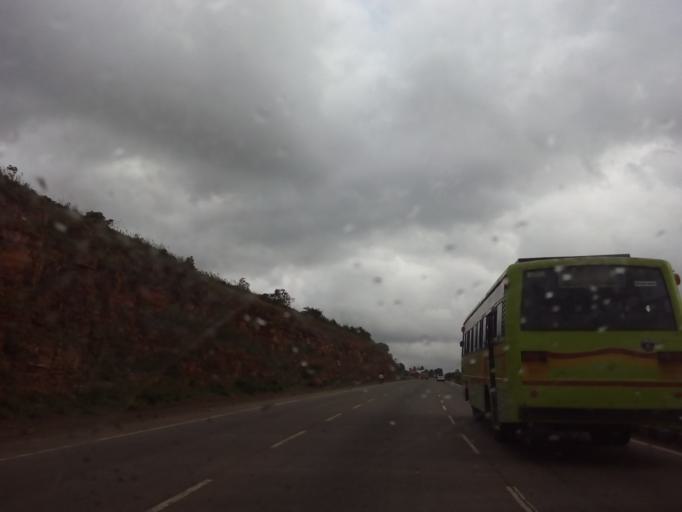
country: IN
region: Karnataka
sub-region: Belgaum
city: Belgaum
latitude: 16.0376
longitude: 74.5309
